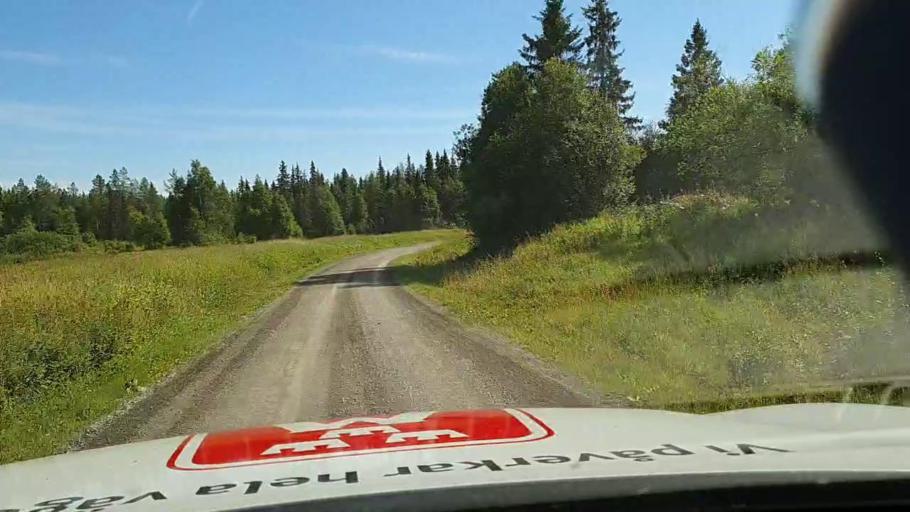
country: SE
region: Jaemtland
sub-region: Stroemsunds Kommun
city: Stroemsund
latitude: 63.7634
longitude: 15.3471
